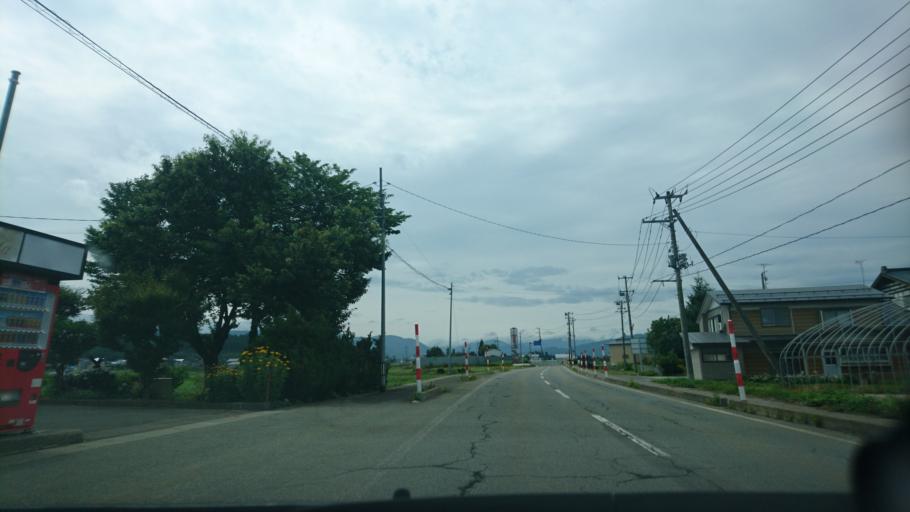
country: JP
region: Akita
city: Yuzawa
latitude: 39.1890
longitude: 140.5514
